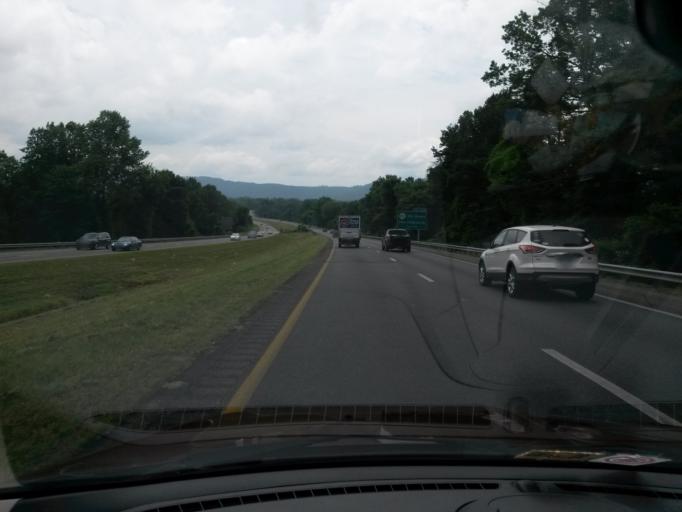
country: US
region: Virginia
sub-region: City of Charlottesville
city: Charlottesville
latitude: 38.0107
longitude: -78.5223
